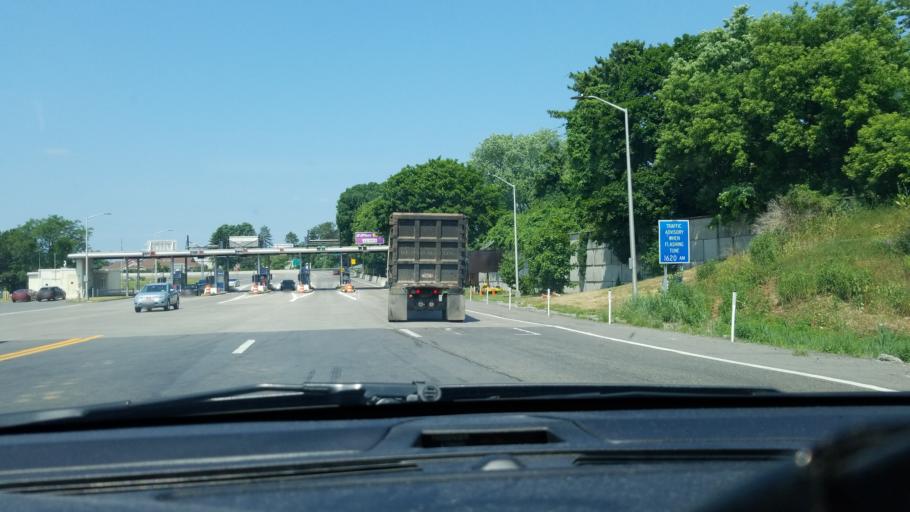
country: US
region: New York
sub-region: Onondaga County
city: Galeville
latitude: 43.0955
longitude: -76.1636
